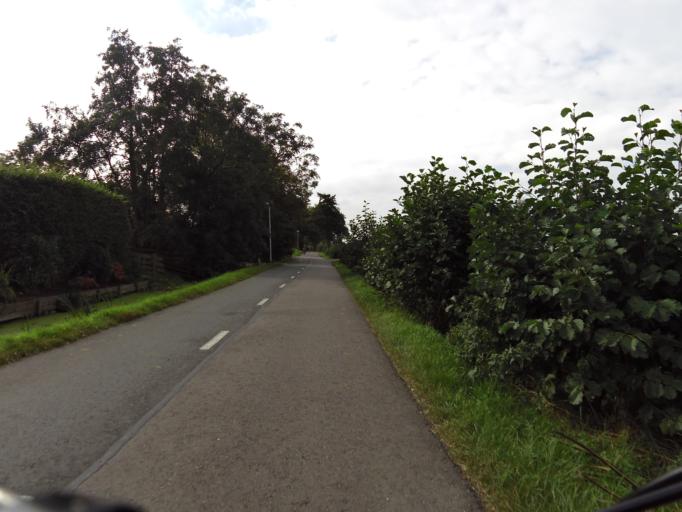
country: NL
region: South Holland
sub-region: Gemeente Rijnwoude
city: Benthuizen
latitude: 52.1115
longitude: 4.5219
